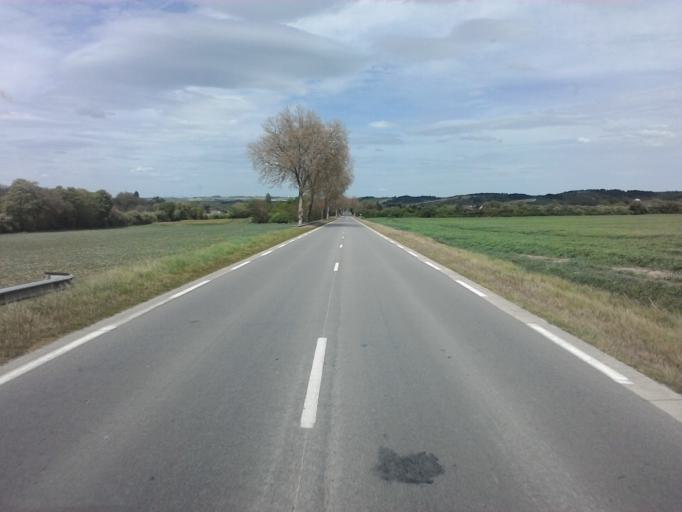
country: FR
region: Bourgogne
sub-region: Departement de l'Yonne
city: Augy
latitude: 47.7557
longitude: 3.6075
